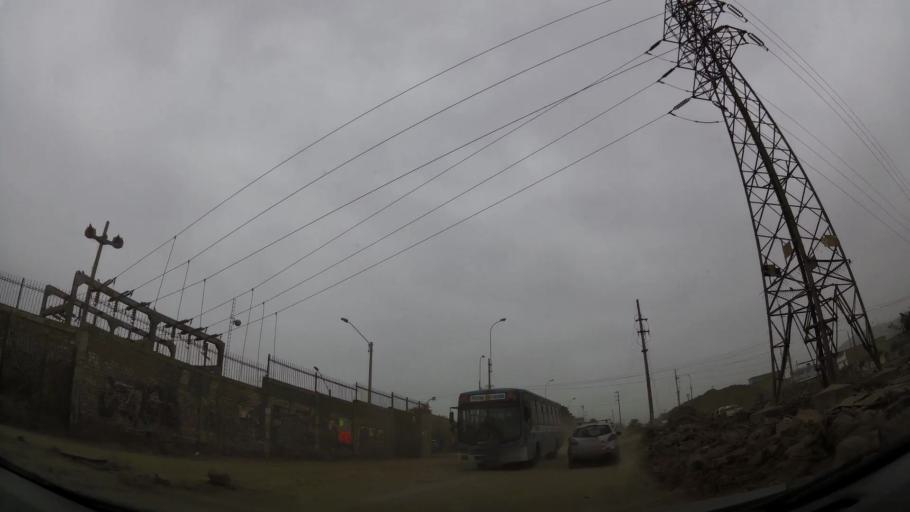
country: PE
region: Lima
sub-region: Lima
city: Surco
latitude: -12.2262
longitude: -76.9224
